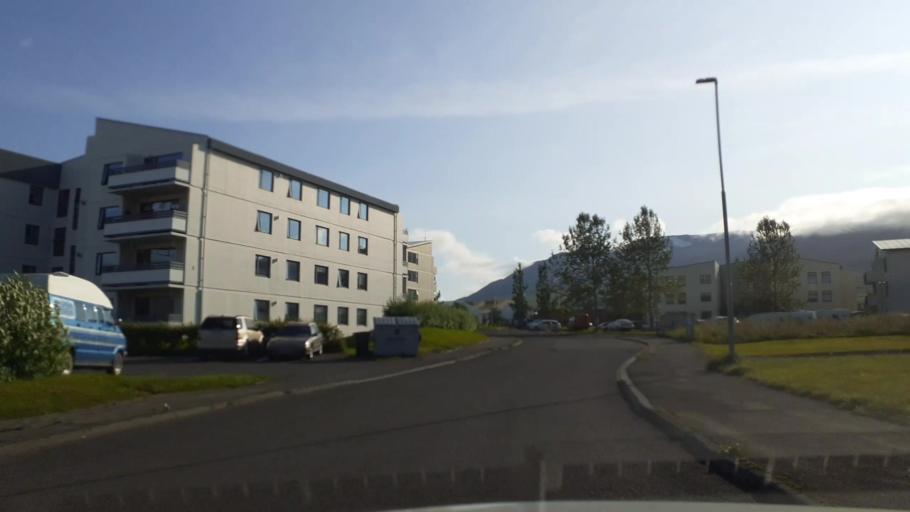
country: IS
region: Northeast
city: Akureyri
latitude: 65.6941
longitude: -18.1351
